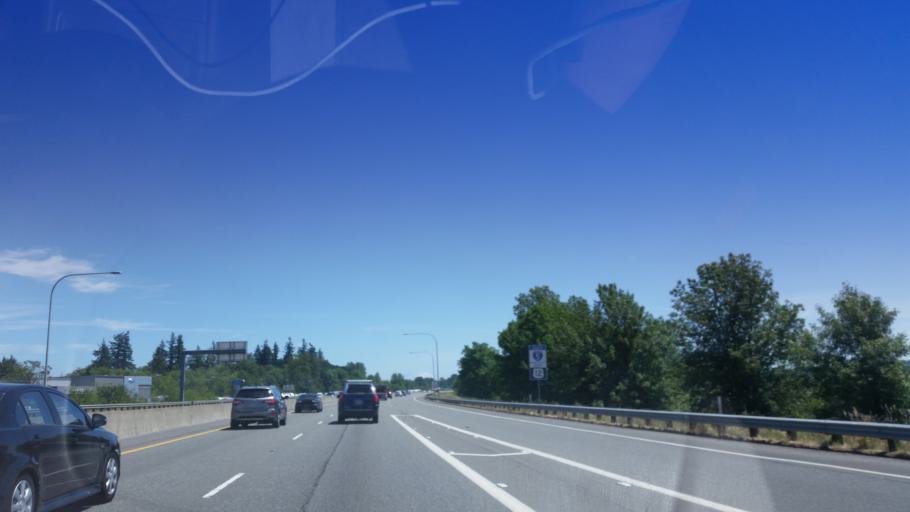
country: US
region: Washington
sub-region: Lewis County
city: Chehalis
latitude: 46.6442
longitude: -122.9558
